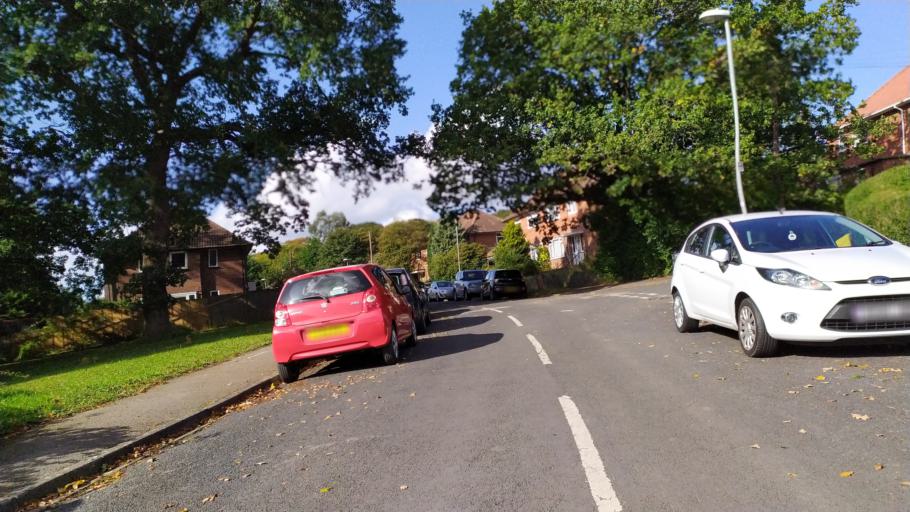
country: GB
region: England
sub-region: City and Borough of Leeds
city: Horsforth
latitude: 53.8222
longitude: -1.5946
